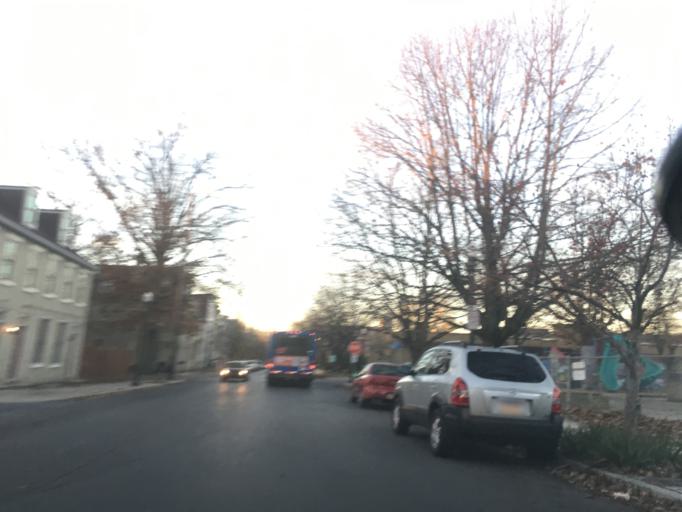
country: US
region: Pennsylvania
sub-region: Dauphin County
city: Harrisburg
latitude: 40.2748
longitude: -76.8927
